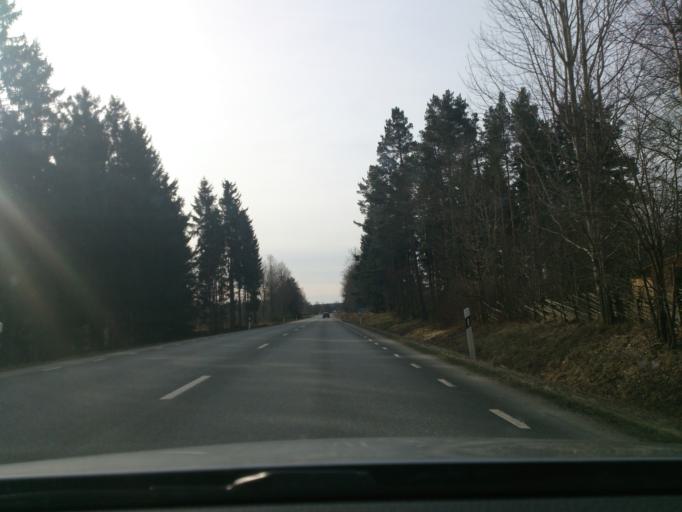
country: SE
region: Kronoberg
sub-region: Alvesta Kommun
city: Moheda
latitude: 56.9690
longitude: 14.5707
